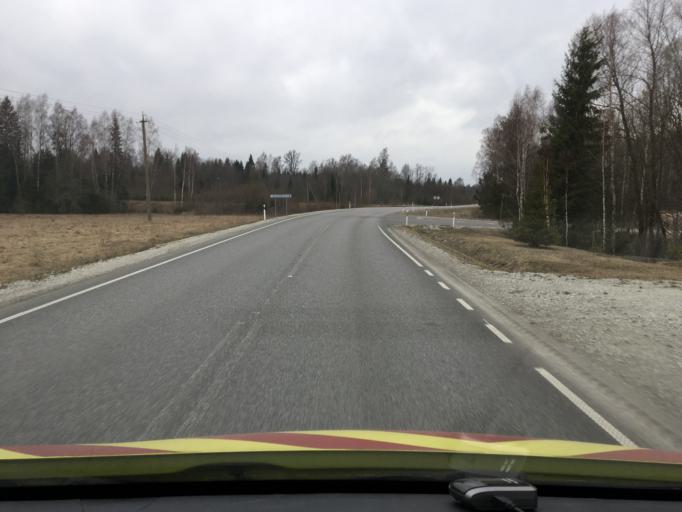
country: EE
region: Raplamaa
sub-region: Rapla vald
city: Rapla
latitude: 59.0094
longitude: 24.8390
